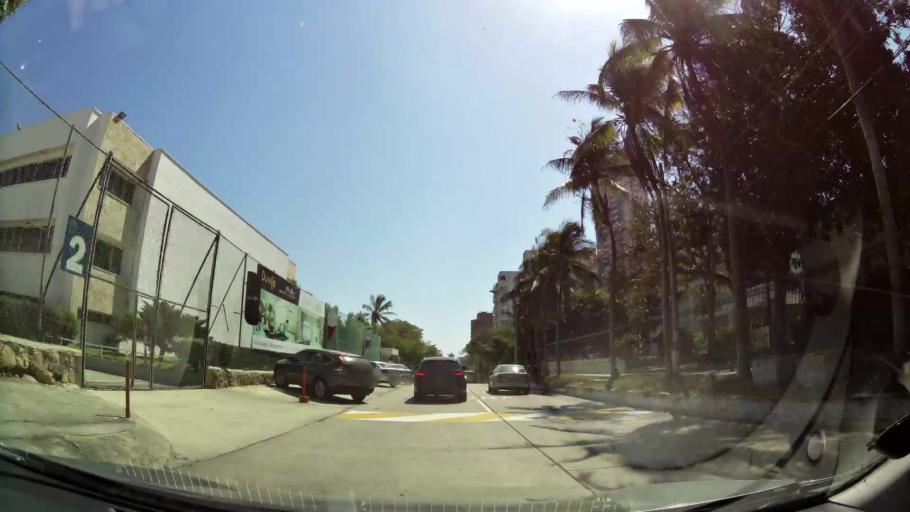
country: CO
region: Atlantico
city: Barranquilla
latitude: 11.0118
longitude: -74.8127
